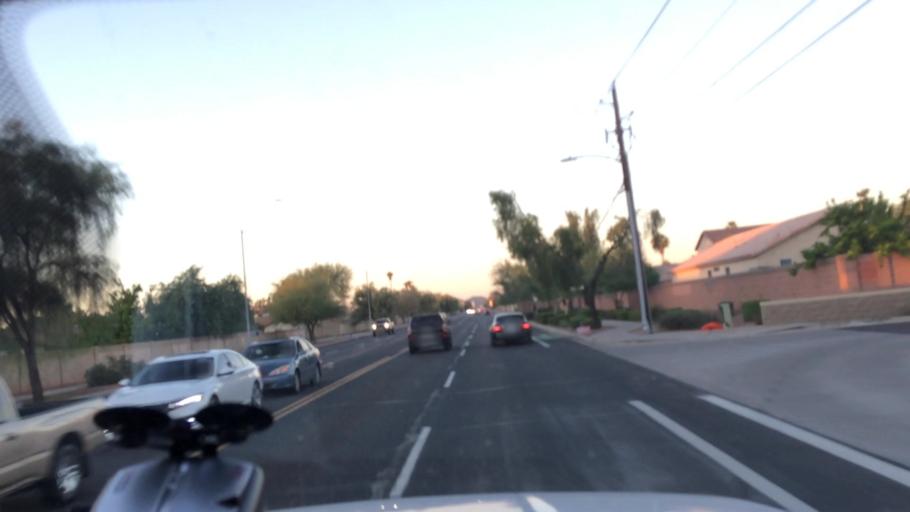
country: US
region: Arizona
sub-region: Maricopa County
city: Glendale
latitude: 33.6552
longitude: -112.0828
